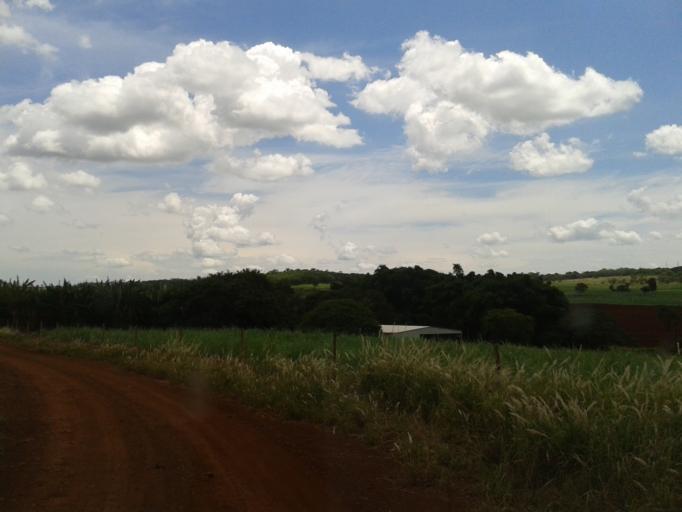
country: BR
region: Minas Gerais
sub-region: Centralina
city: Centralina
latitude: -18.6821
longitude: -49.2340
